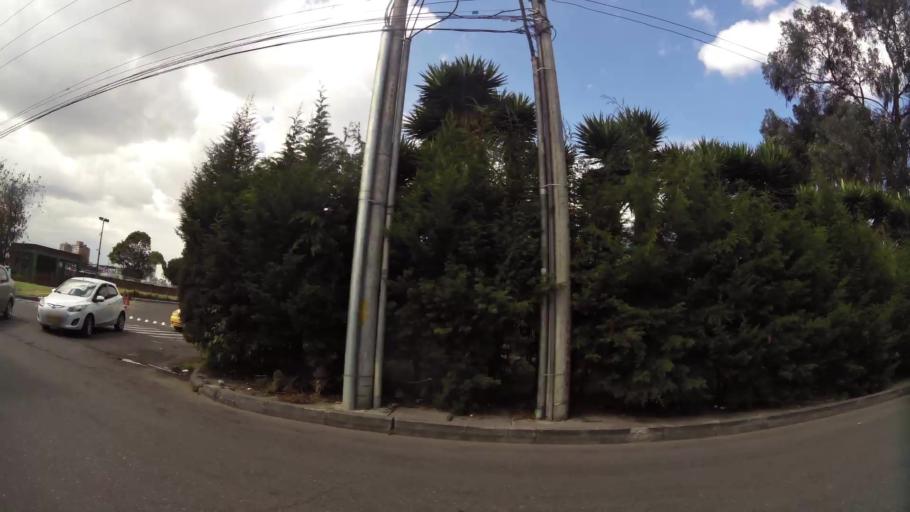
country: CO
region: Bogota D.C.
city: Bogota
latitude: 4.6334
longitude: -74.1028
